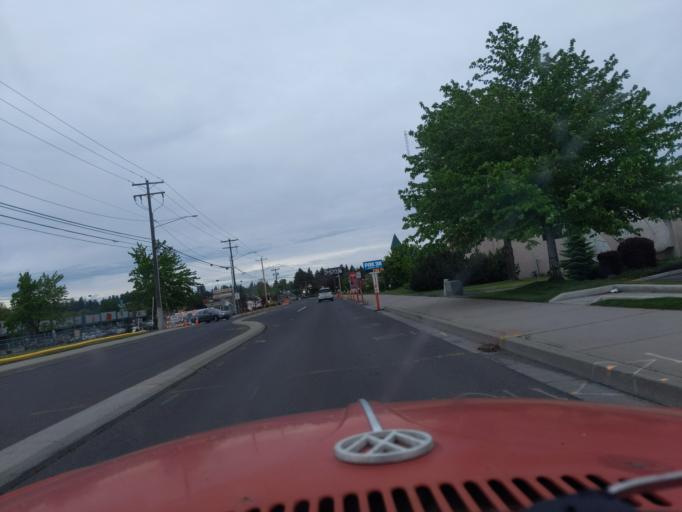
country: US
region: Washington
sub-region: Spokane County
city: Spokane
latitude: 47.6108
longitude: -117.3681
